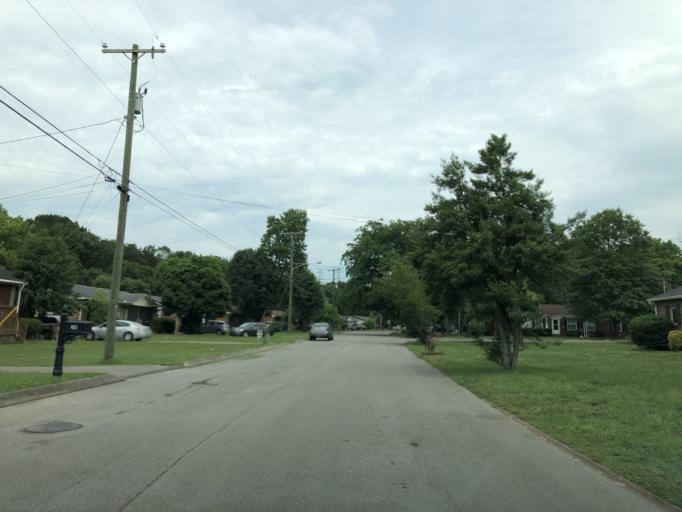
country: US
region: Tennessee
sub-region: Davidson County
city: Goodlettsville
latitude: 36.2856
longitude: -86.7122
